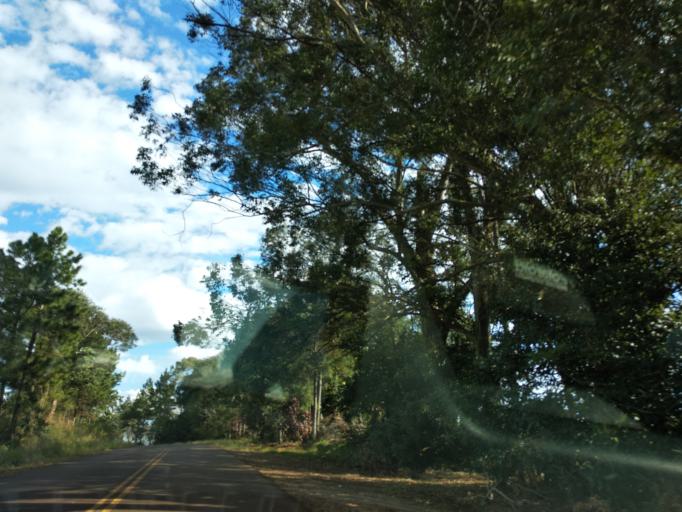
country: AR
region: Misiones
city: Aristobulo del Valle
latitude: -27.0731
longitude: -54.8315
